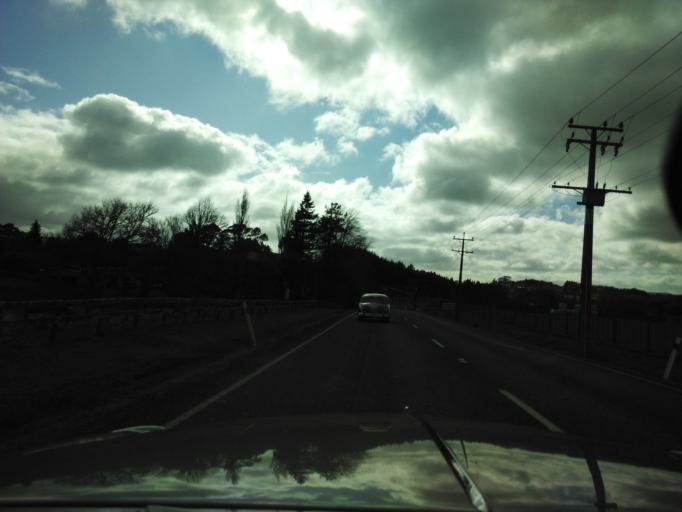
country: NZ
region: Auckland
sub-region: Auckland
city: Pukekohe East
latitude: -37.1438
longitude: 175.0365
